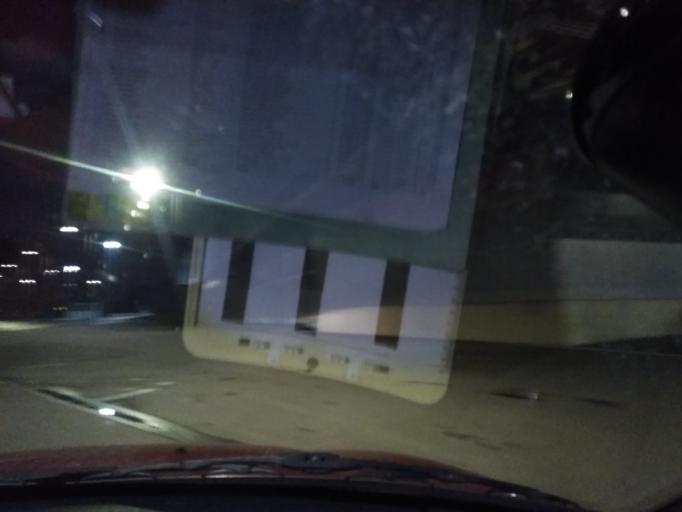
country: AT
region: Lower Austria
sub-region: Politischer Bezirk Wien-Umgebung
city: Leopoldsdorf
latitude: 48.1626
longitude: 16.3889
